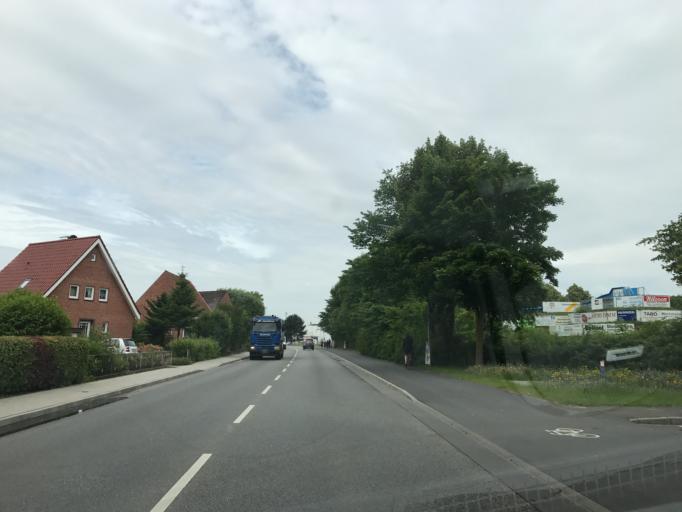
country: DE
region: Schleswig-Holstein
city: Meldorf
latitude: 54.0956
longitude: 9.0679
